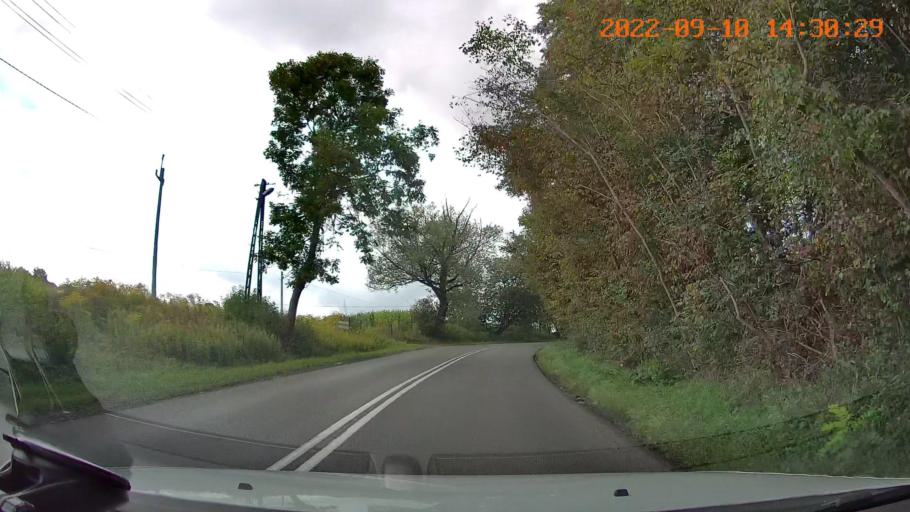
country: PL
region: Lesser Poland Voivodeship
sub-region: Powiat krakowski
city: Kryspinow
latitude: 50.0660
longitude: 19.8219
